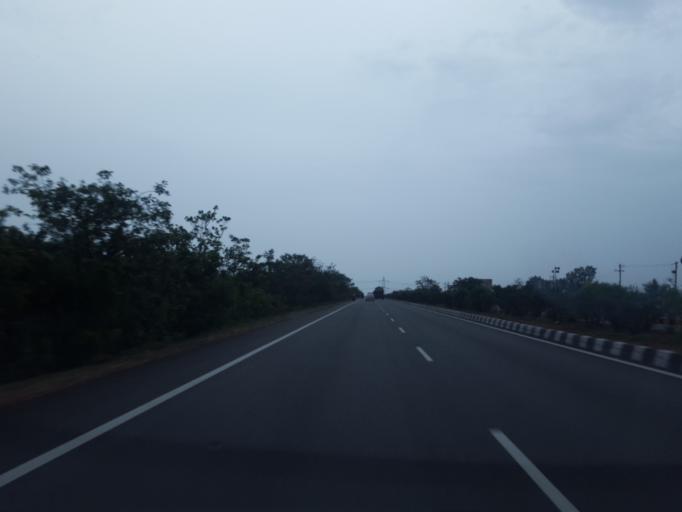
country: IN
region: Telangana
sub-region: Mahbubnagar
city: Farrukhnagar
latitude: 17.0916
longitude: 78.2411
